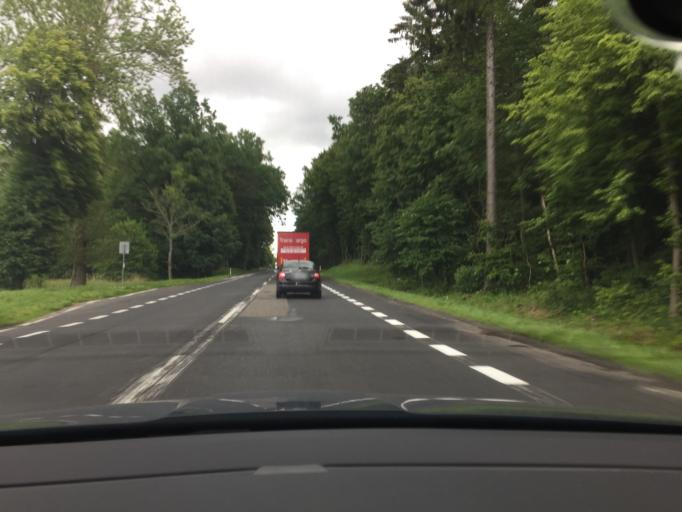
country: PL
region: West Pomeranian Voivodeship
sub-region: Powiat bialogardzki
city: Bialogard
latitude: 54.0779
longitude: 15.9701
